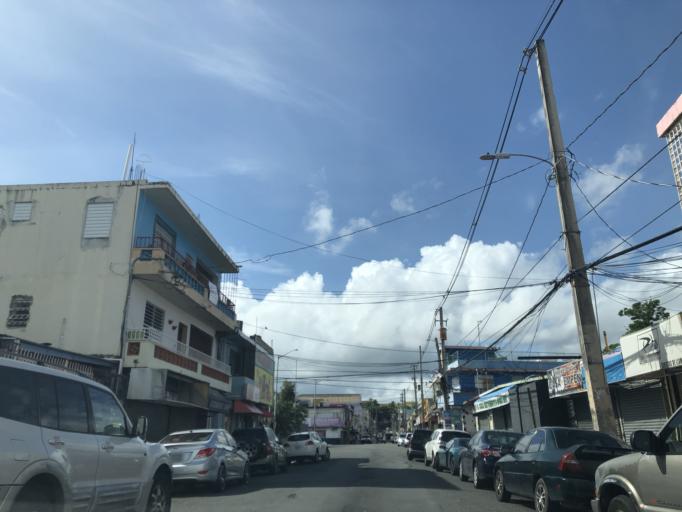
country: PR
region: Trujillo Alto
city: Trujillo Alto
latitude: 18.4006
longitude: -66.0460
